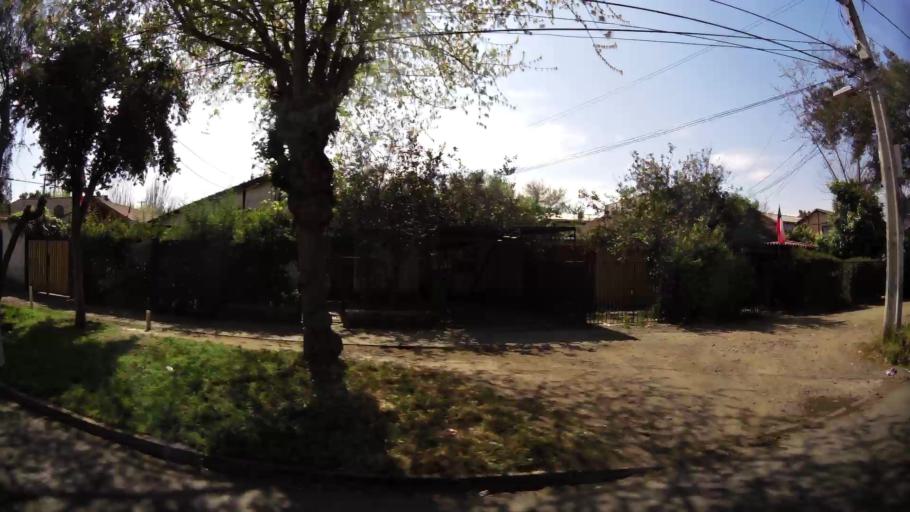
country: CL
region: Santiago Metropolitan
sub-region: Provincia de Santiago
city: Lo Prado
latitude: -33.4710
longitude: -70.7270
